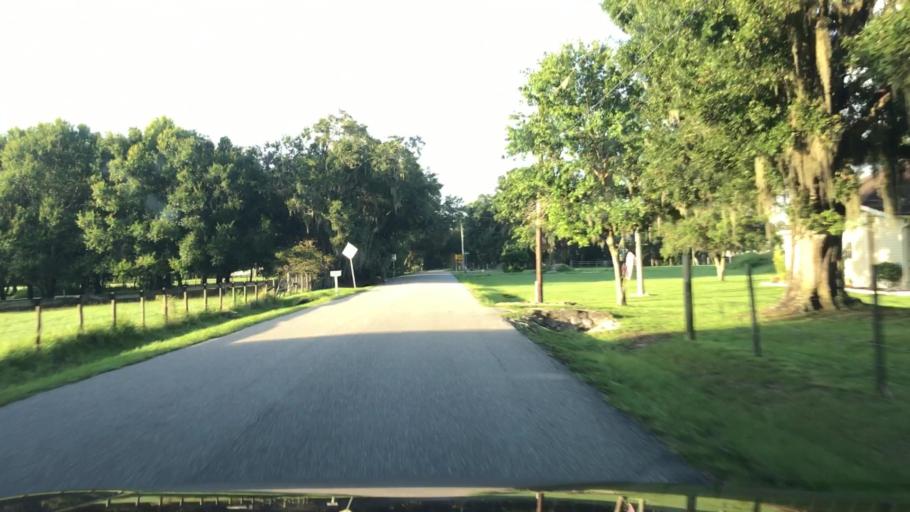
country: US
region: Florida
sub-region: Sarasota County
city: Lake Sarasota
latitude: 27.3322
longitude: -82.4083
